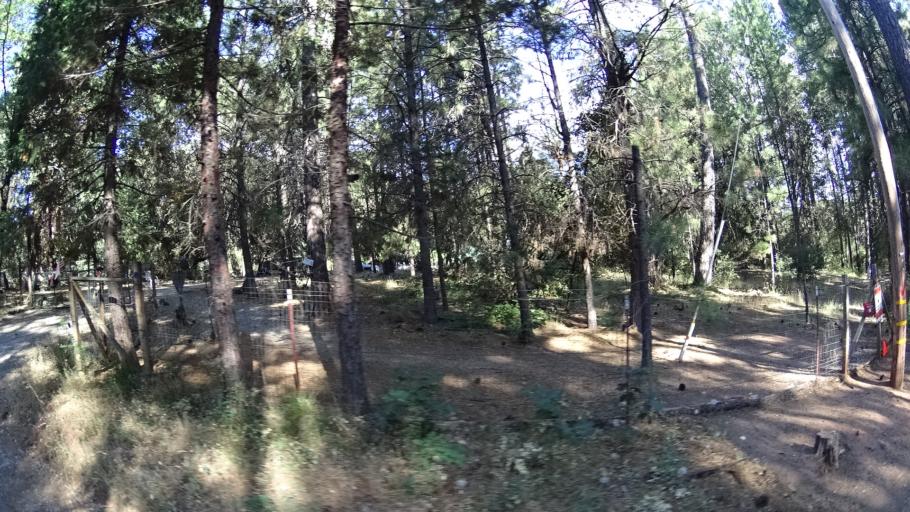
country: US
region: California
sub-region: Amador County
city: Pioneer
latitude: 38.3845
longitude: -120.5560
